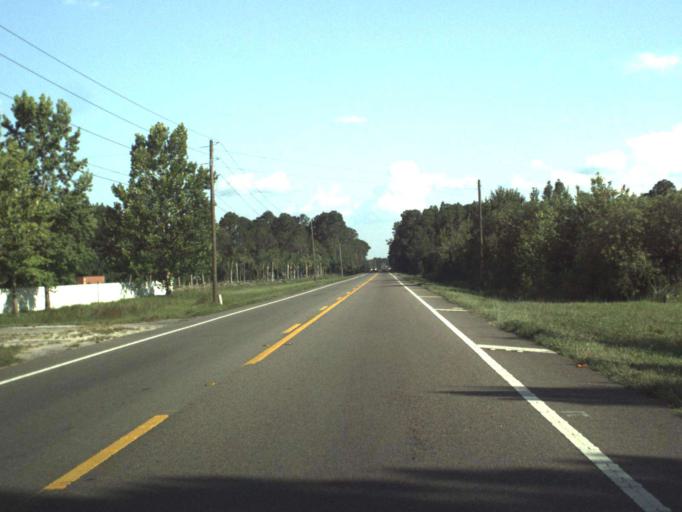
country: US
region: Florida
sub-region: Lake County
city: Clermont
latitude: 28.4012
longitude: -81.8281
